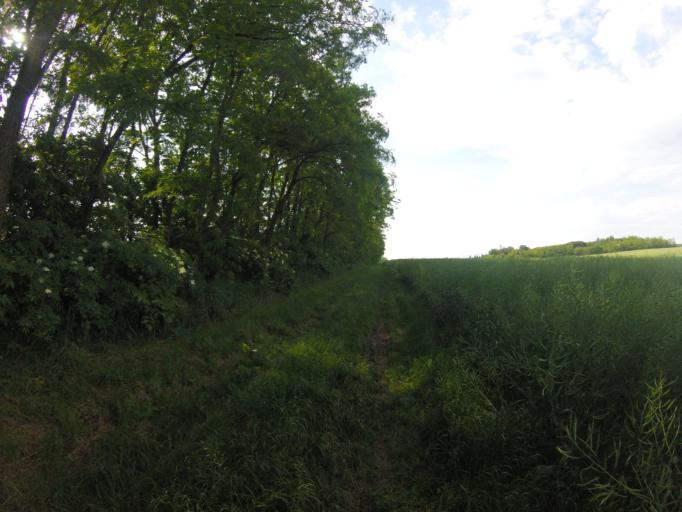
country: HU
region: Zala
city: Zalaszentgrot
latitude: 46.8717
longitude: 17.1192
